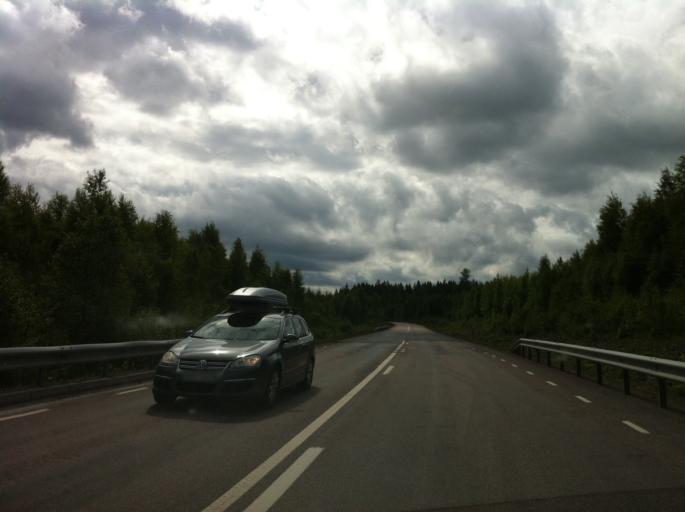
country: SE
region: Vaermland
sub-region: Sunne Kommun
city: Sunne
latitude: 59.7724
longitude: 13.0966
